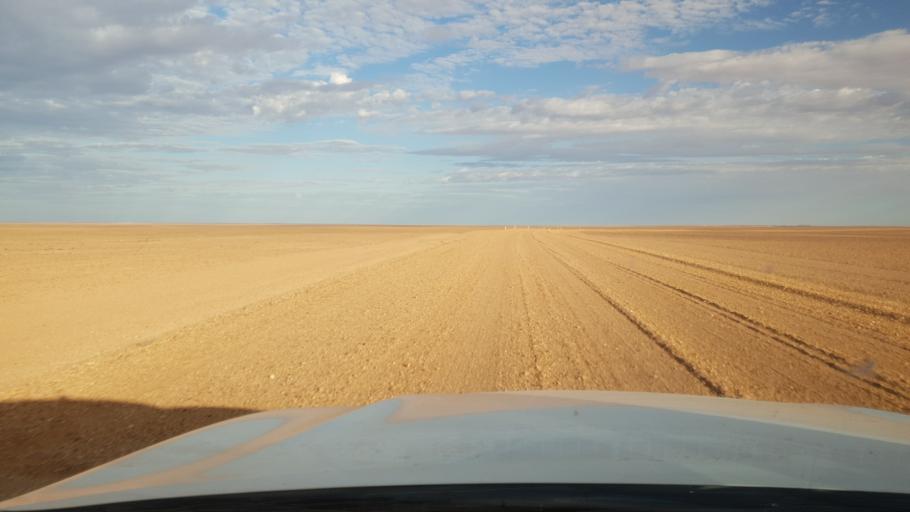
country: AU
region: South Australia
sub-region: Coober Pedy
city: Coober Pedy
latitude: -28.6619
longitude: 134.9482
